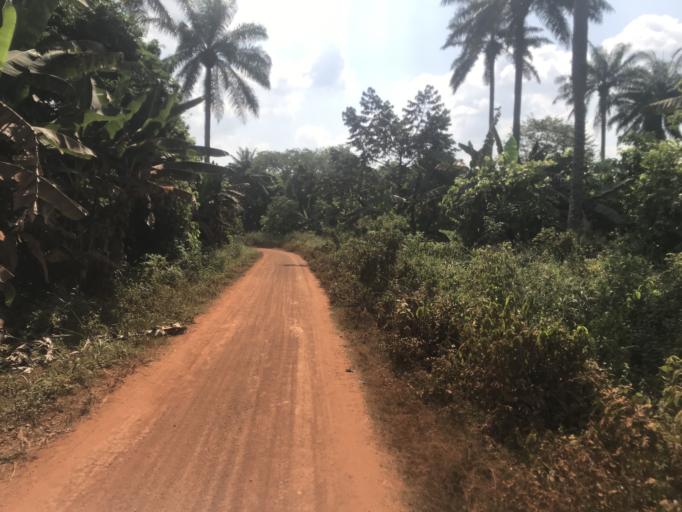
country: NG
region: Osun
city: Ibokun
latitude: 7.8024
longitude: 4.6873
